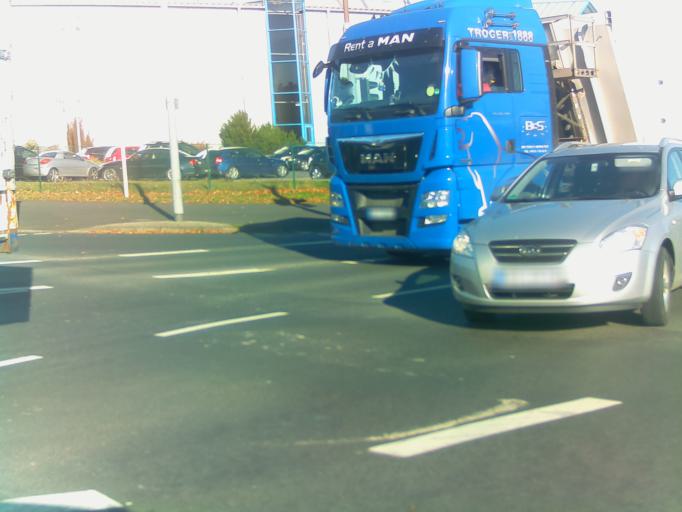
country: DE
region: Bavaria
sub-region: Regierungsbezirk Unterfranken
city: Bad Neustadt an der Saale
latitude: 50.3305
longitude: 10.2196
